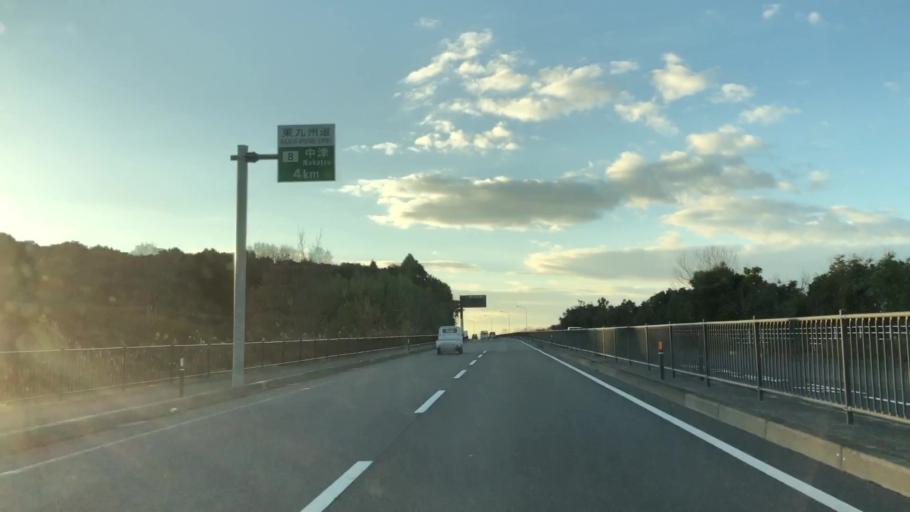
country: JP
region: Fukuoka
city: Nakatsu
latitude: 33.5538
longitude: 131.2563
